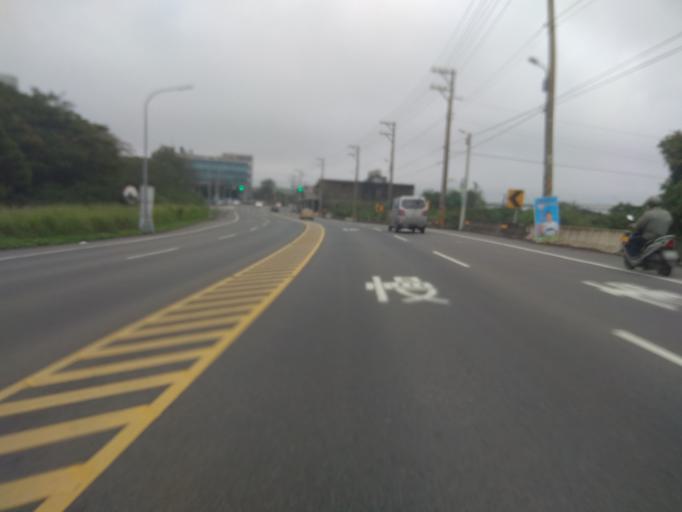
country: TW
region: Taiwan
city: Taoyuan City
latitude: 25.0207
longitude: 121.1210
